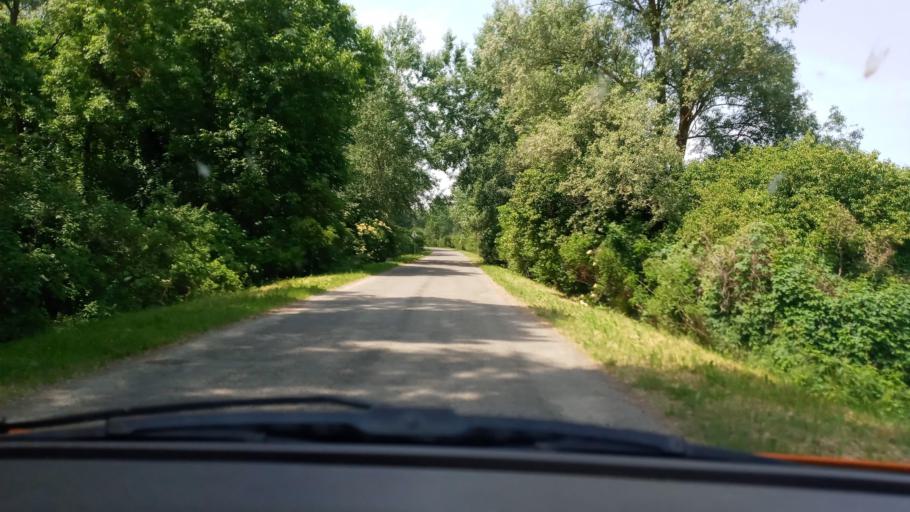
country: HU
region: Baranya
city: Sellye
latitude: 45.8066
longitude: 17.8813
